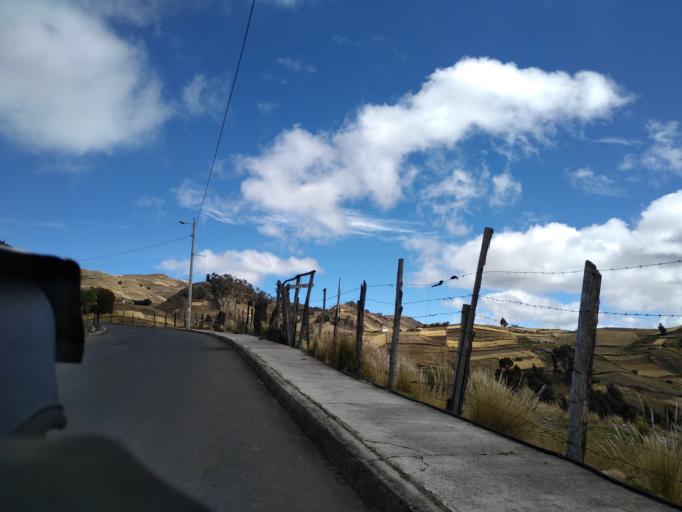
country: EC
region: Cotopaxi
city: Pujili
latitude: -0.9631
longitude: -78.9007
